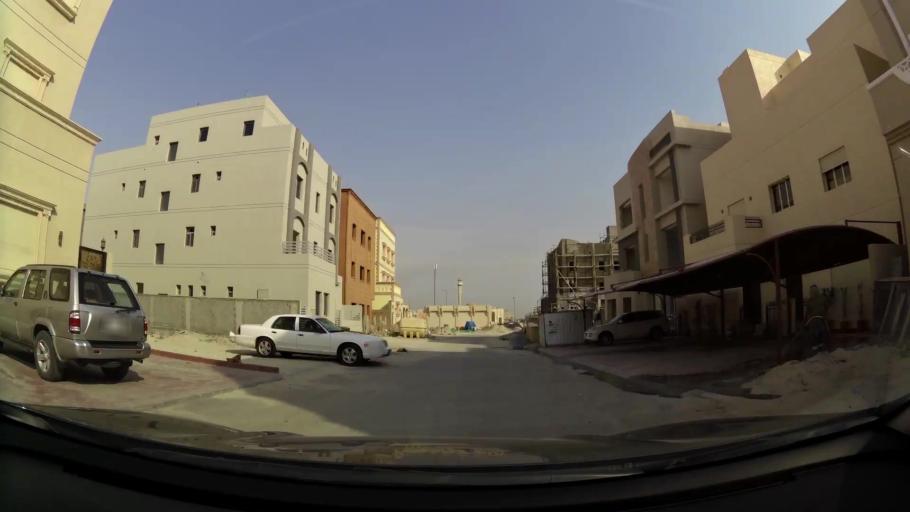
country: KW
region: Al Asimah
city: Ar Rabiyah
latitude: 29.3301
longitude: 47.8033
